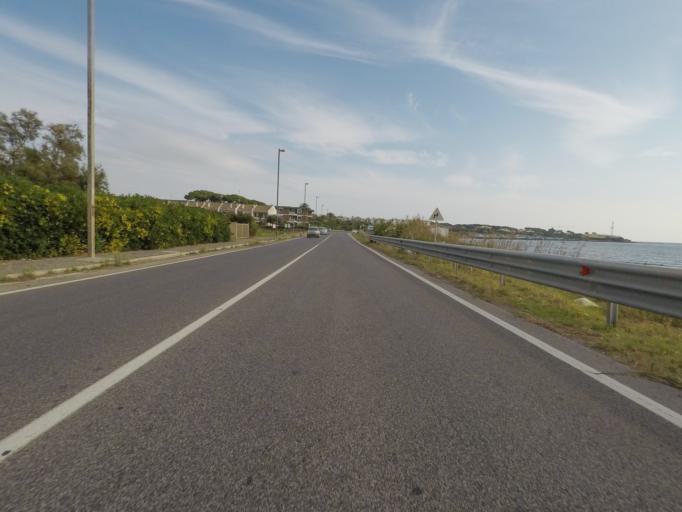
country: IT
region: Latium
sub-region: Citta metropolitana di Roma Capitale
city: Santa Marinella
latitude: 42.0393
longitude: 11.8303
